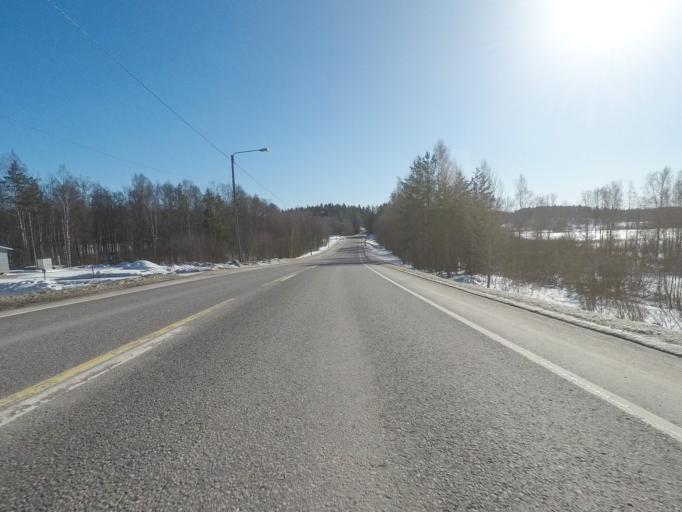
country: FI
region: Uusimaa
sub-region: Helsinki
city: Espoo
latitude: 60.2423
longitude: 24.5847
